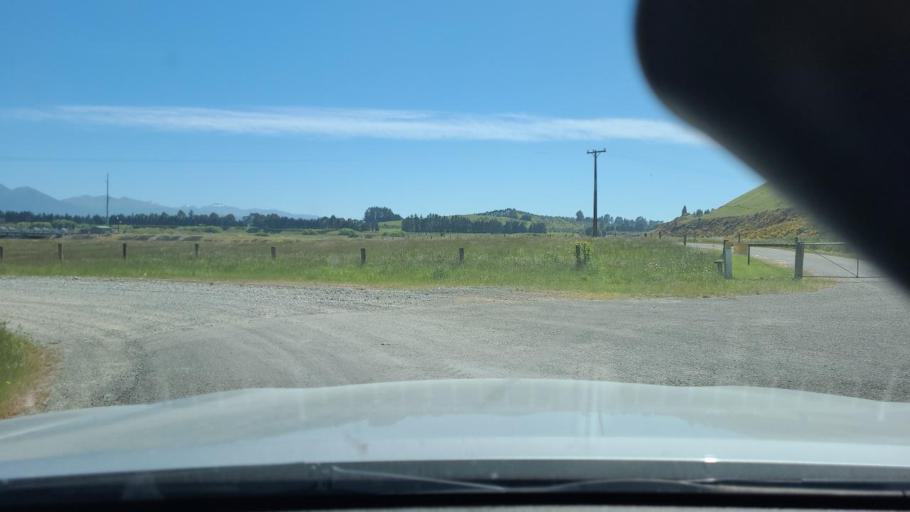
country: NZ
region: Southland
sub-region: Southland District
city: Te Anau
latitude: -45.6183
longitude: 167.6940
